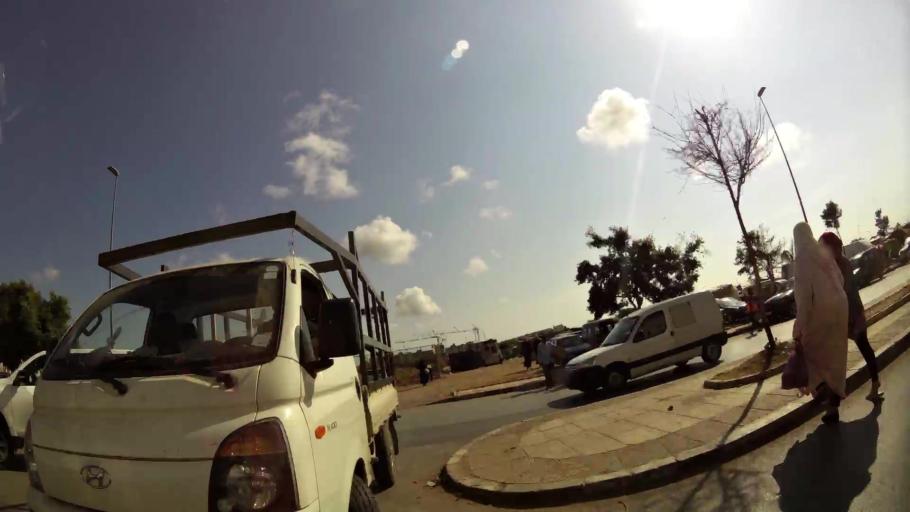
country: MA
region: Rabat-Sale-Zemmour-Zaer
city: Sale
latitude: 34.0497
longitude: -6.7884
